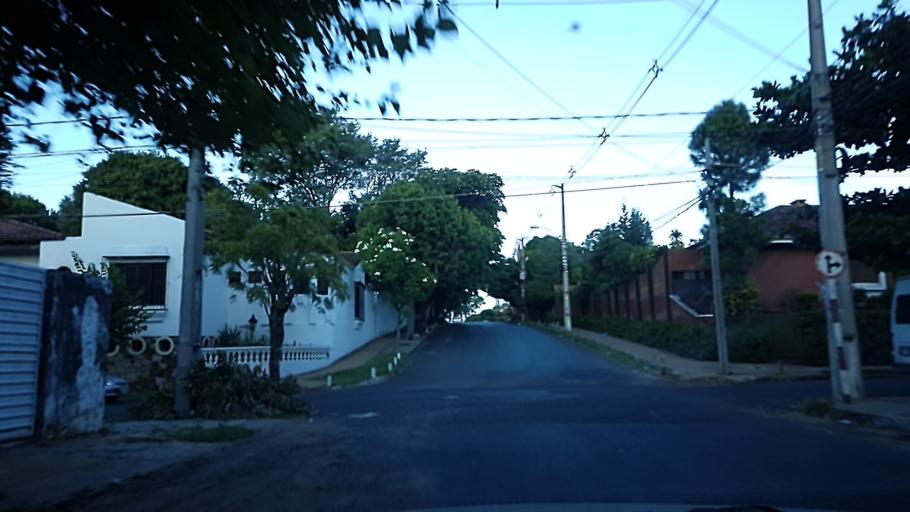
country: PY
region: Asuncion
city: Asuncion
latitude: -25.2838
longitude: -57.6028
